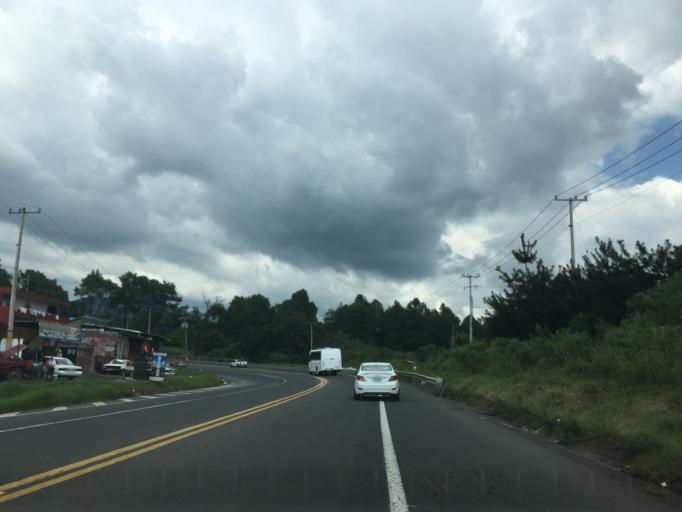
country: MX
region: Michoacan
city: Capacuaro
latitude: 19.4811
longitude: -102.0693
